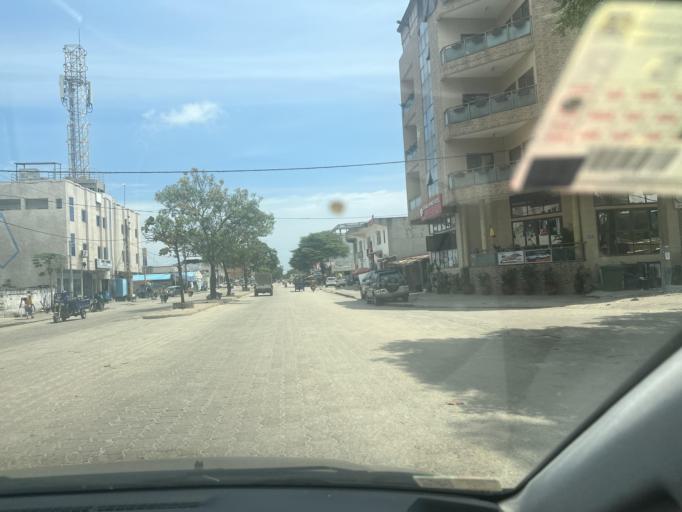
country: BJ
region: Littoral
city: Cotonou
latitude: 6.3806
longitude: 2.4469
